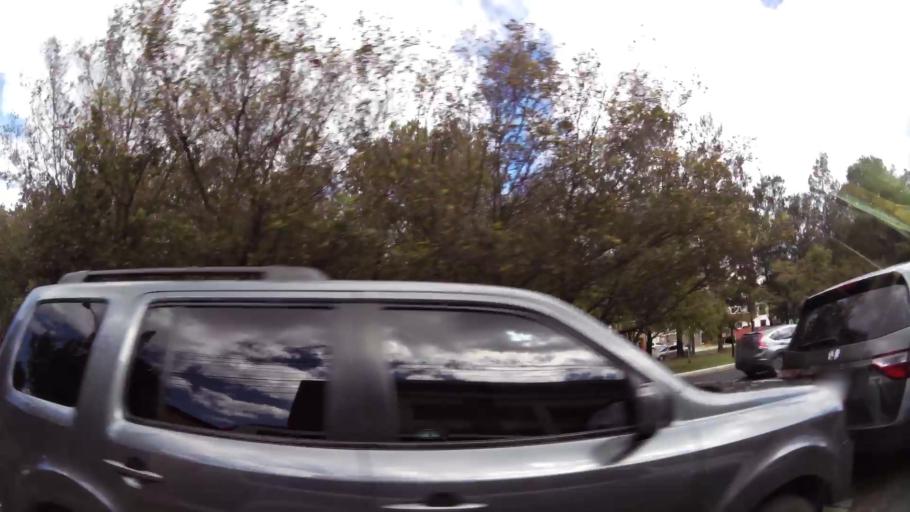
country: GT
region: Guatemala
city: Santa Catarina Pinula
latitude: 14.5869
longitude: -90.4892
